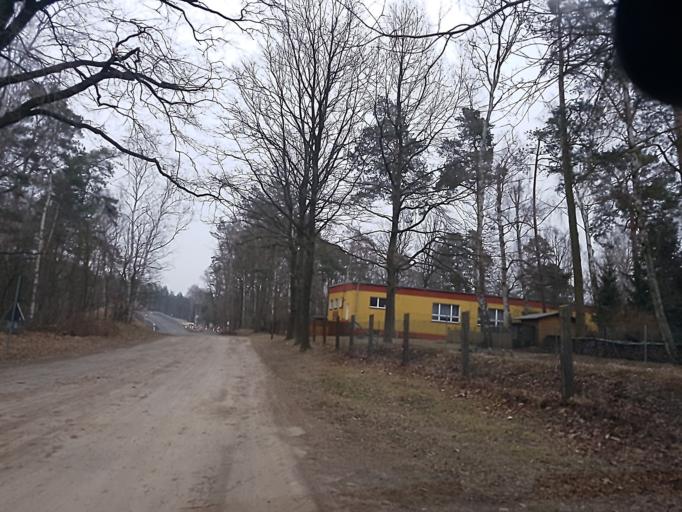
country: DE
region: Brandenburg
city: Ruckersdorf
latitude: 51.5941
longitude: 13.5649
